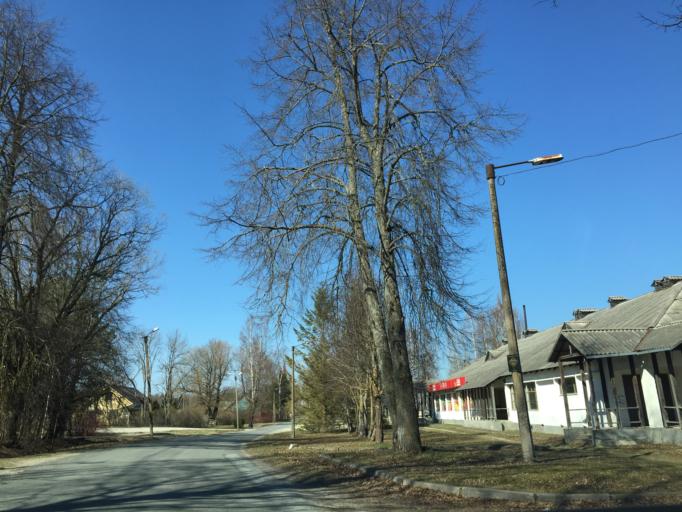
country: EE
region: Jogevamaa
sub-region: Mustvee linn
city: Mustvee
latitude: 58.9472
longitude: 27.0484
